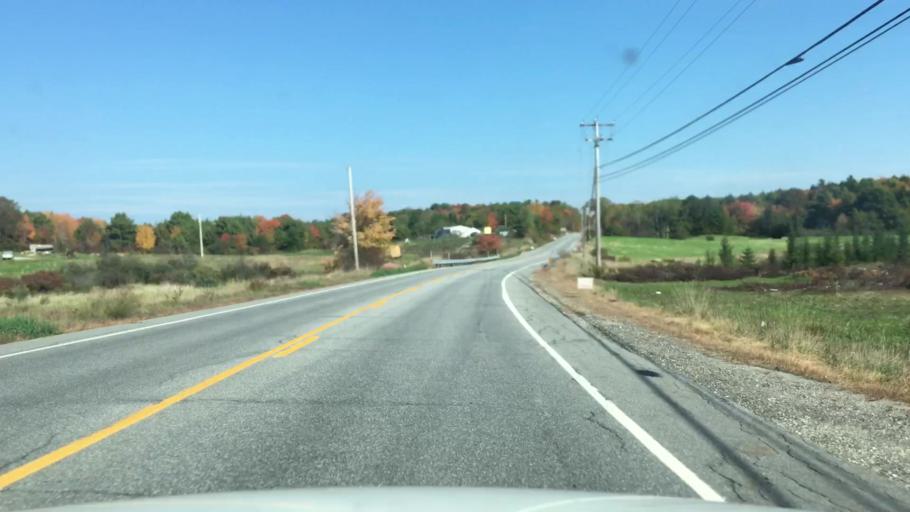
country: US
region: Maine
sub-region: Sagadahoc County
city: Topsham
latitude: 43.9813
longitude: -69.9605
